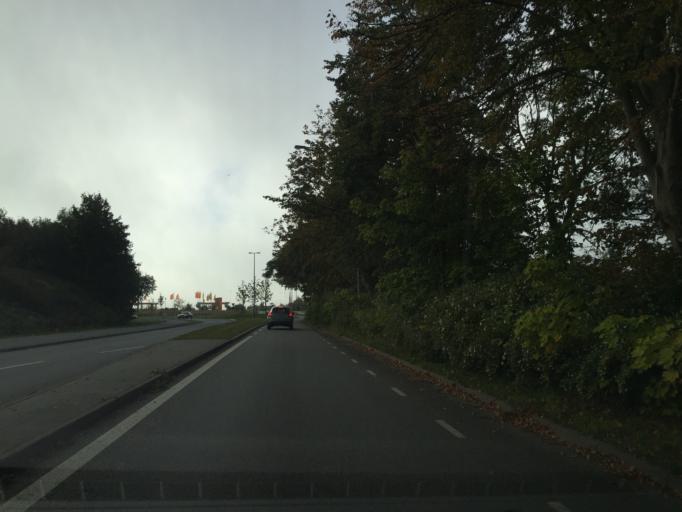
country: SE
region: Skane
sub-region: Staffanstorps Kommun
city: Staffanstorp
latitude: 55.6327
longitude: 13.1860
